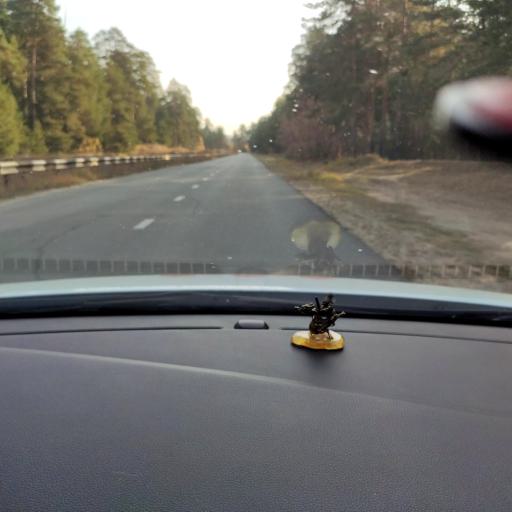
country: RU
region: Tatarstan
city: Osinovo
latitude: 55.8249
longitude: 48.9073
